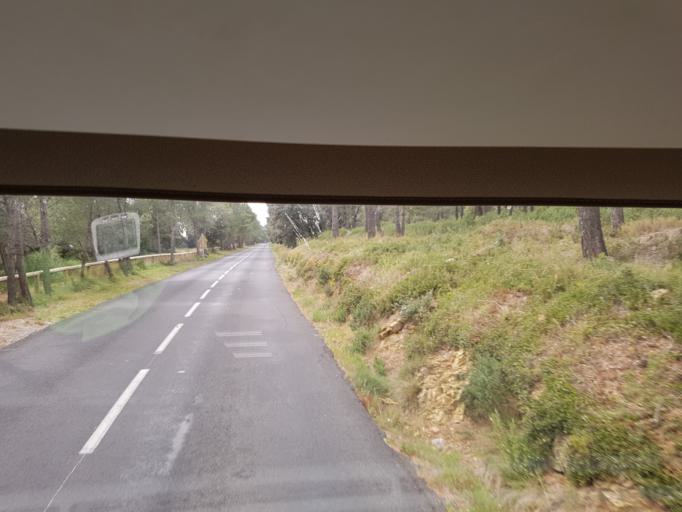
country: FR
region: Languedoc-Roussillon
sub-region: Departement de l'Aude
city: Fleury
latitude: 43.1990
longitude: 3.1607
